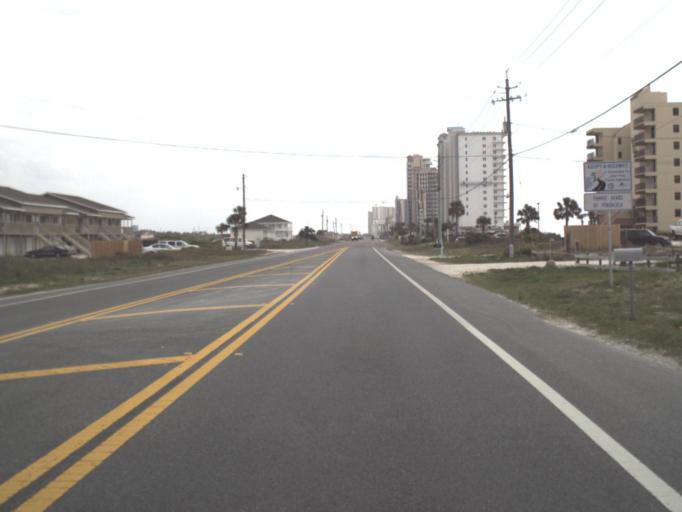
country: US
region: Alabama
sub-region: Baldwin County
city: Orange Beach
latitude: 30.2943
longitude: -87.4500
